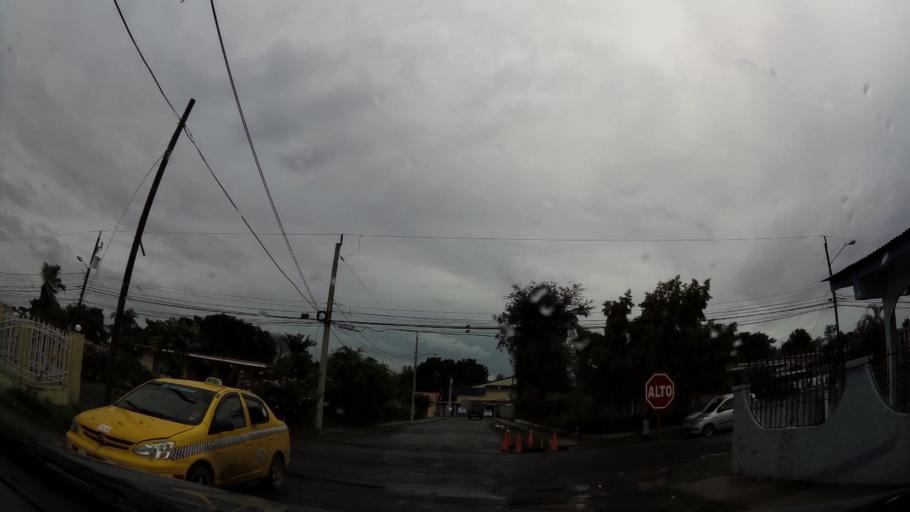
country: PA
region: Veraguas
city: Santiago de Veraguas
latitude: 8.1042
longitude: -80.9719
